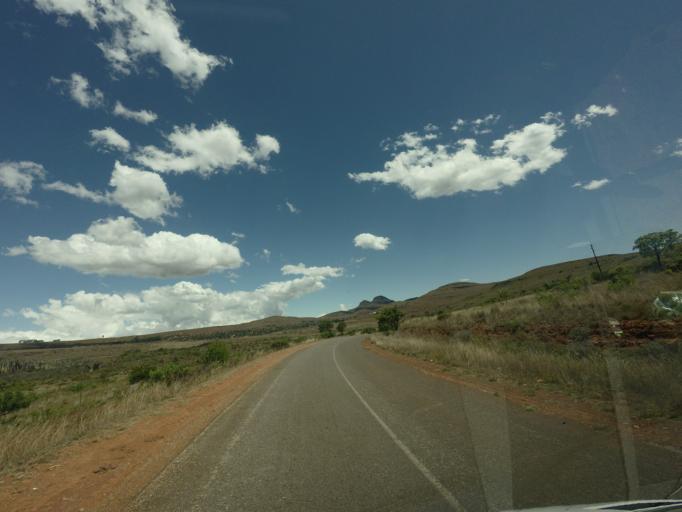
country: ZA
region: Limpopo
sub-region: Mopani District Municipality
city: Hoedspruit
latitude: -24.5969
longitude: 30.7889
